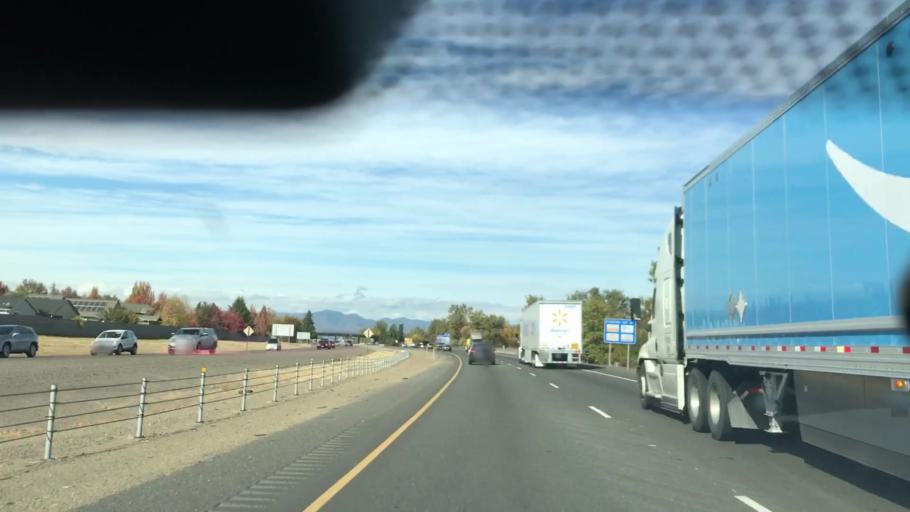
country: US
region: Oregon
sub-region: Jackson County
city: Medford
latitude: 42.3586
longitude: -122.8802
